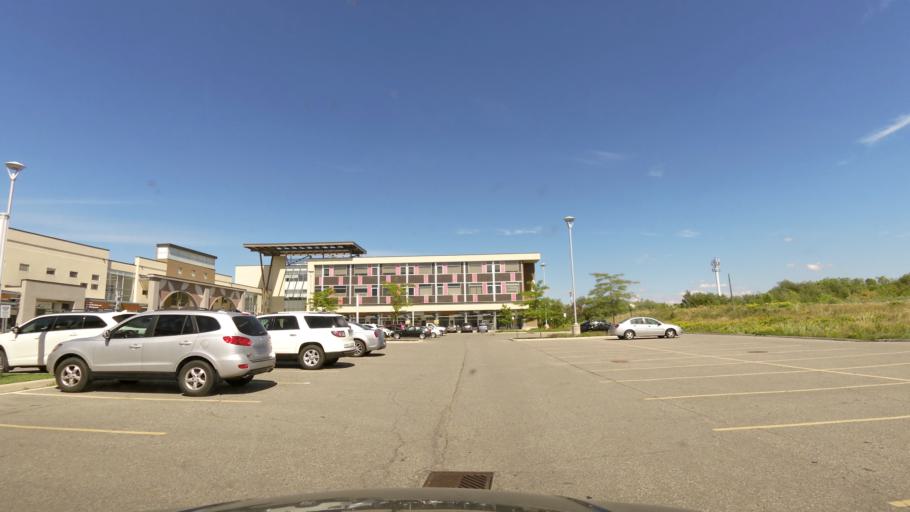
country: CA
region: Ontario
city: Mississauga
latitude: 43.6272
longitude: -79.6270
